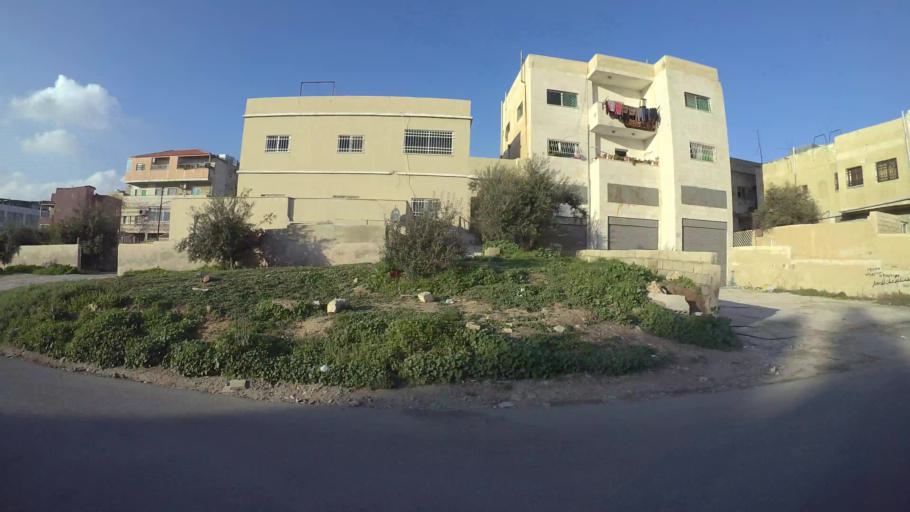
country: JO
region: Amman
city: Al Bunayyat ash Shamaliyah
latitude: 31.9093
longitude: 35.9141
